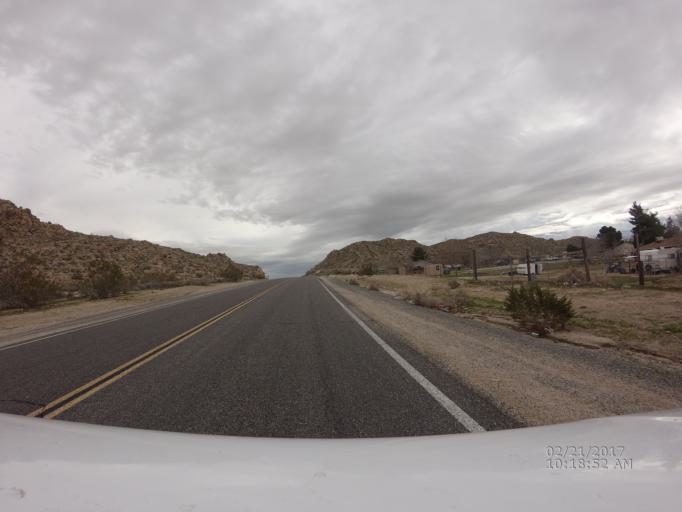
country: US
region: California
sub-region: Los Angeles County
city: Lake Los Angeles
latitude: 34.6070
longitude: -117.8220
